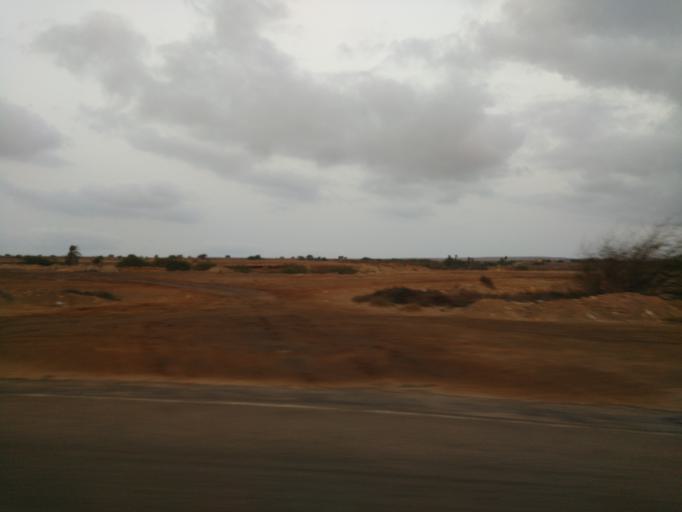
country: CV
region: Sal
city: Espargos
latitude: 16.6789
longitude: -22.9335
